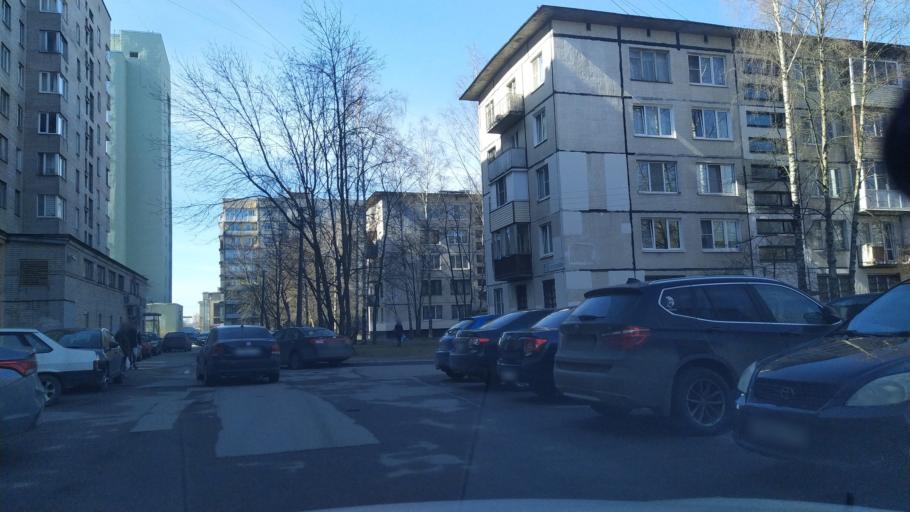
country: RU
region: St.-Petersburg
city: Grazhdanka
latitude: 60.0373
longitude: 30.4147
